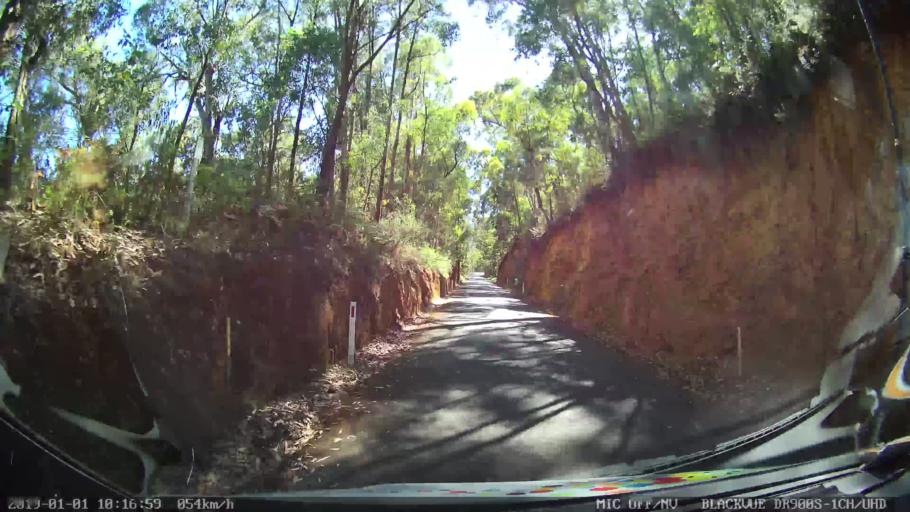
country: AU
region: New South Wales
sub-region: Snowy River
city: Jindabyne
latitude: -36.0922
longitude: 148.1723
